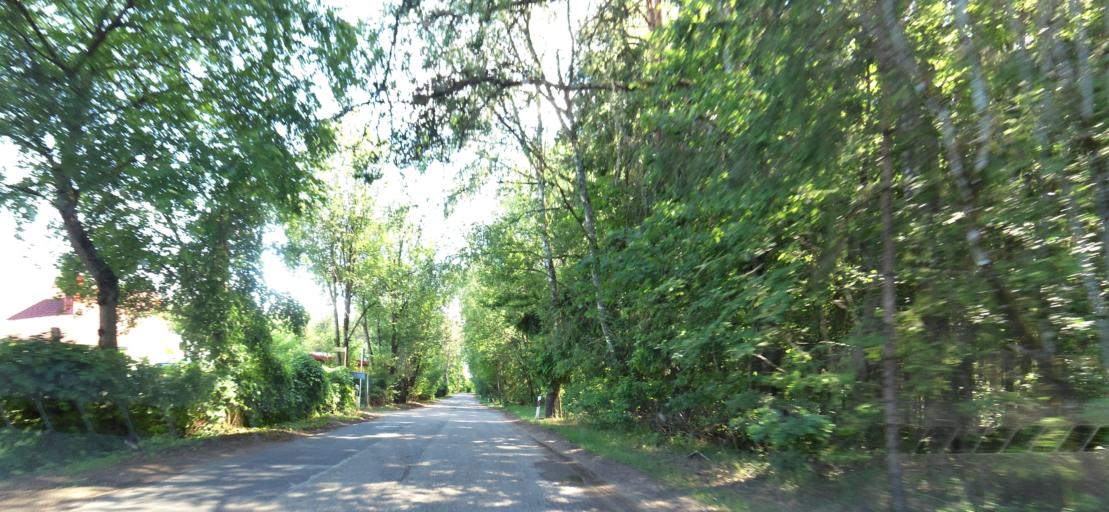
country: LT
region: Vilnius County
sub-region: Vilnius
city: Fabijoniskes
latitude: 54.8196
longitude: 25.3209
